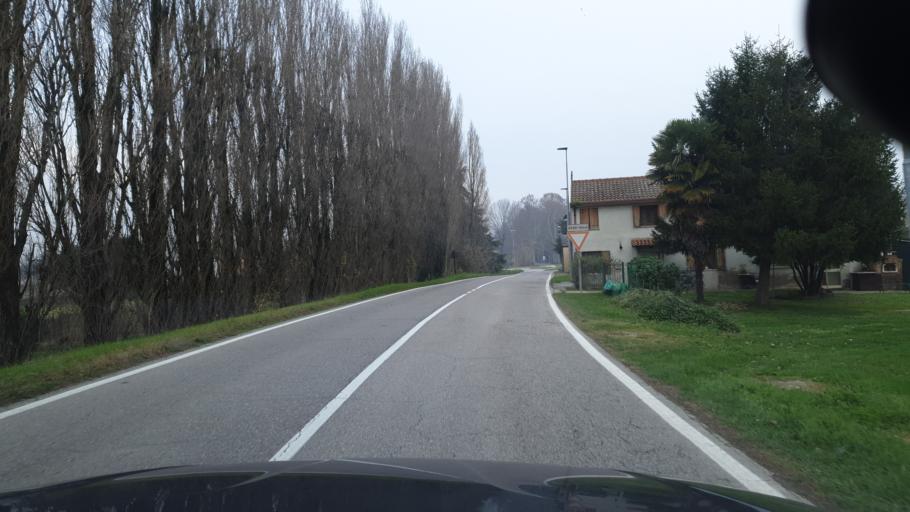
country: IT
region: Veneto
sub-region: Provincia di Rovigo
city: Fratta Polesine
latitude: 45.0261
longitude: 11.6397
